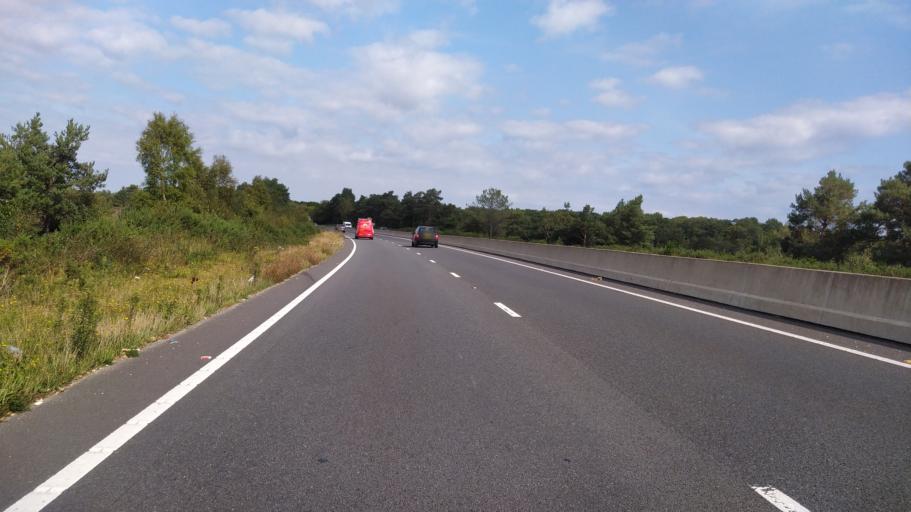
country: GB
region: England
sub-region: Dorset
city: Christchurch
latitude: 50.7716
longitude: -1.8067
